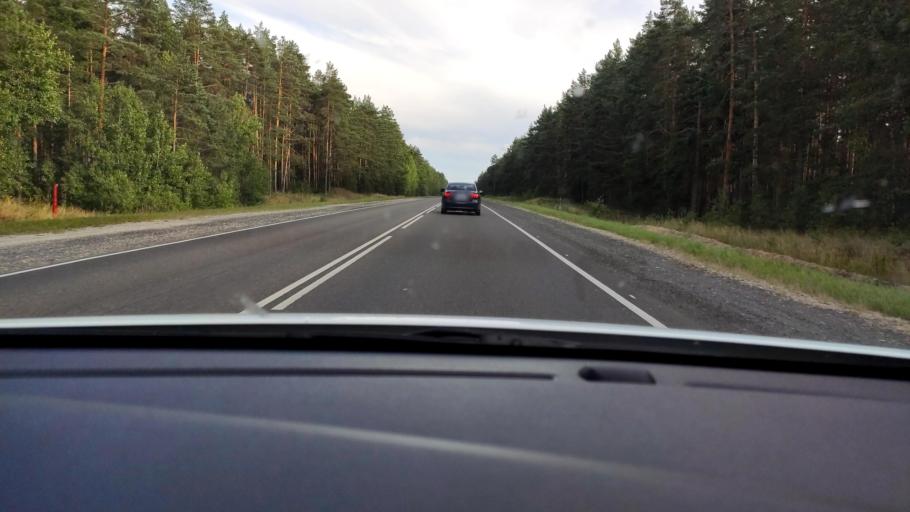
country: RU
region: Mariy-El
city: Suslonger
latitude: 56.3646
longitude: 48.2148
